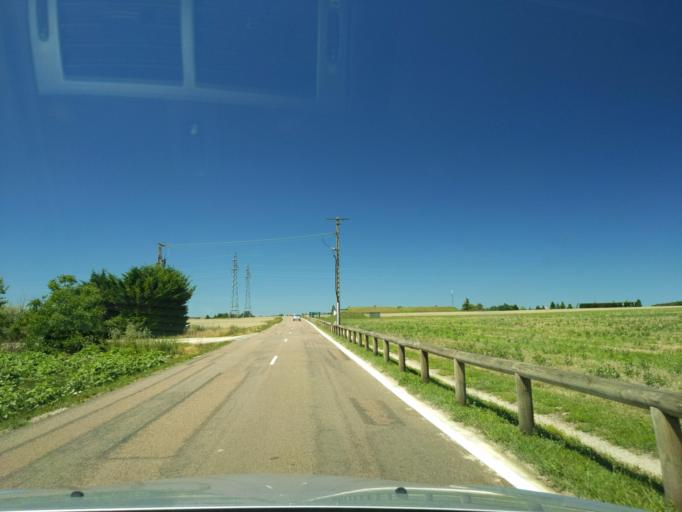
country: FR
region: Bourgogne
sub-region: Departement de la Cote-d'Or
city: Ruffey-les-Echirey
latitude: 47.3821
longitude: 5.0602
